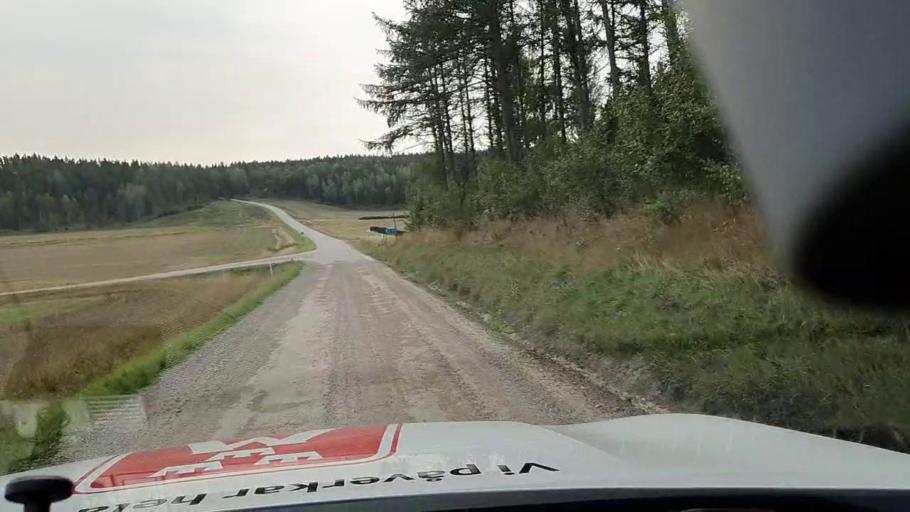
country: SE
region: Soedermanland
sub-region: Nykopings Kommun
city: Nykoping
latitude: 58.8976
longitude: 16.9883
